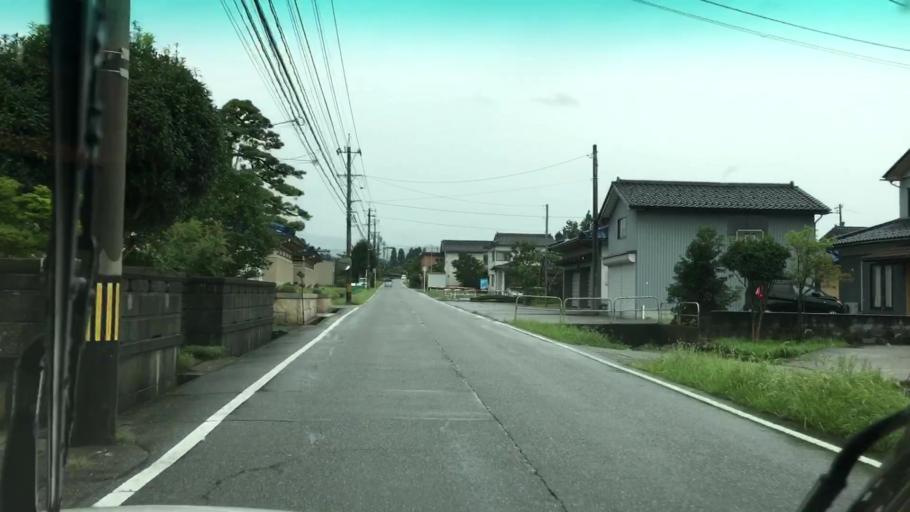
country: JP
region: Toyama
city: Kamiichi
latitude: 36.6445
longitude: 137.3202
